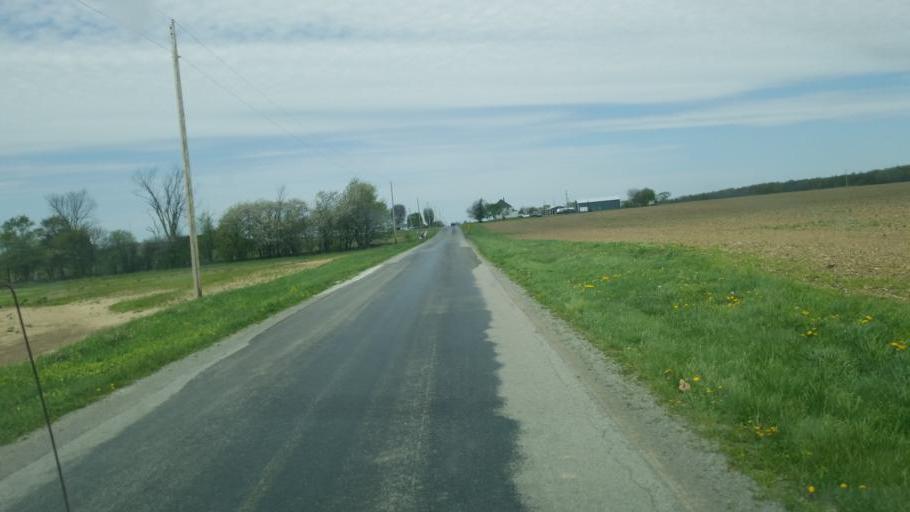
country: US
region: Ohio
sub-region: Hardin County
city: Ada
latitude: 40.8138
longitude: -83.8800
